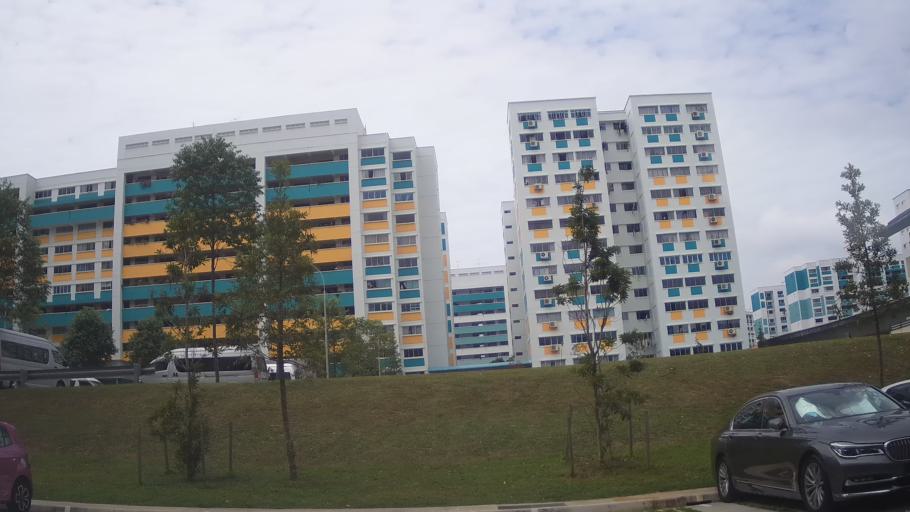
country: MY
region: Johor
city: Johor Bahru
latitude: 1.3762
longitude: 103.7718
